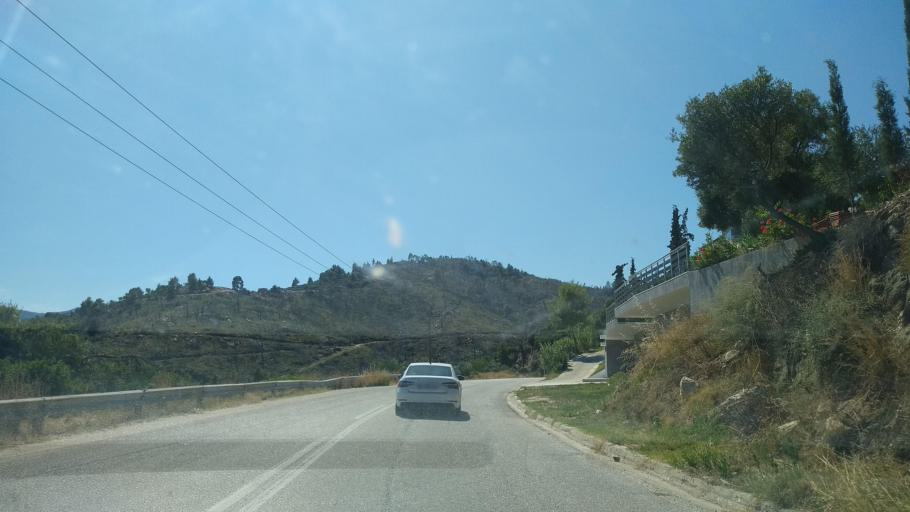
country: GR
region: Central Macedonia
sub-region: Nomos Chalkidikis
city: Sarti
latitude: 40.1048
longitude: 23.9831
